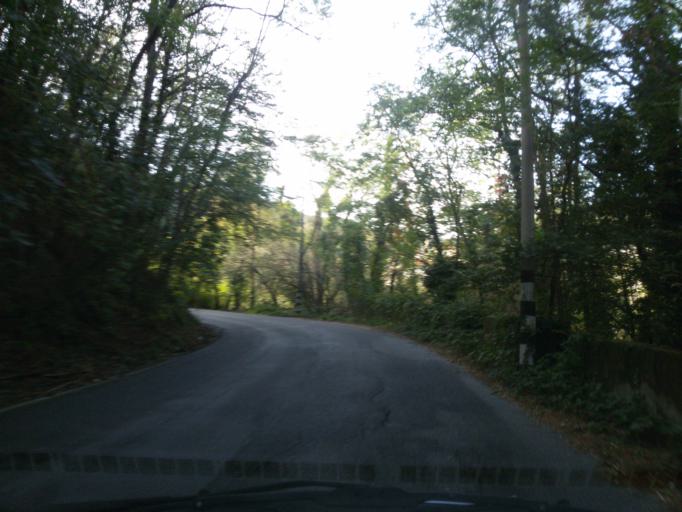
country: IT
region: Liguria
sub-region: Provincia di Genova
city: Piccarello
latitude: 44.4643
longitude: 8.9676
